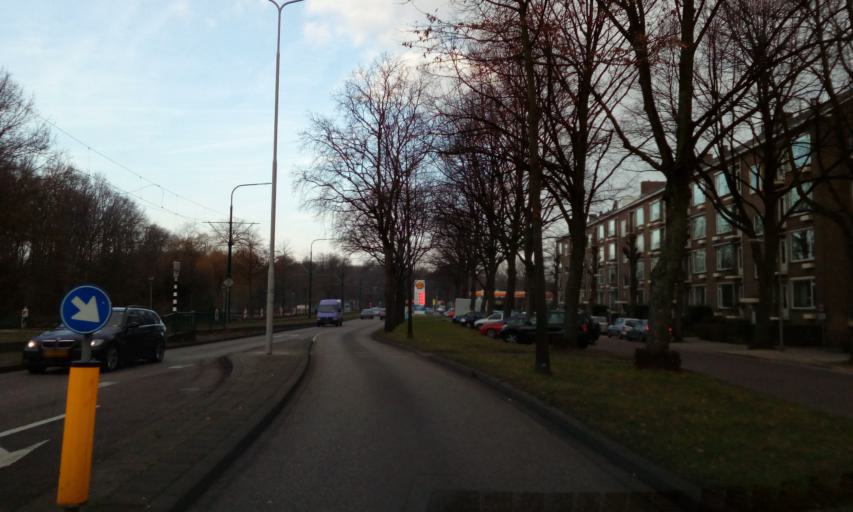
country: NL
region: South Holland
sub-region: Gemeente Rijswijk
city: Rijswijk
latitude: 52.0505
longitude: 4.3293
